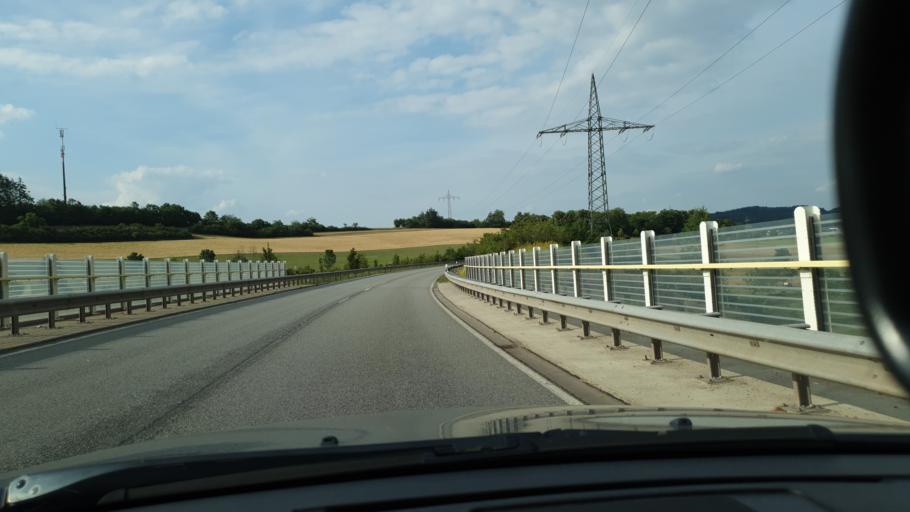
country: DE
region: Rheinland-Pfalz
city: Katzweiler
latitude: 49.4824
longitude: 7.7044
